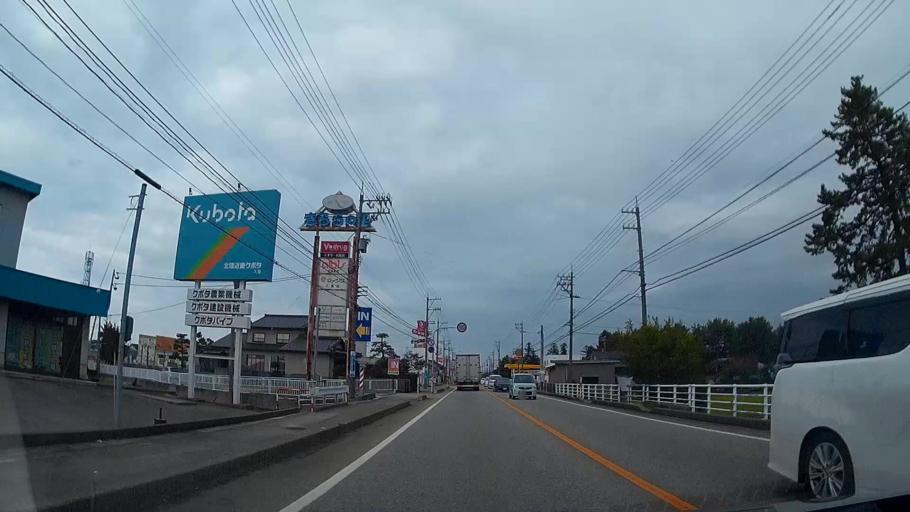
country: JP
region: Toyama
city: Nyuzen
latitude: 36.9295
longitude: 137.4983
